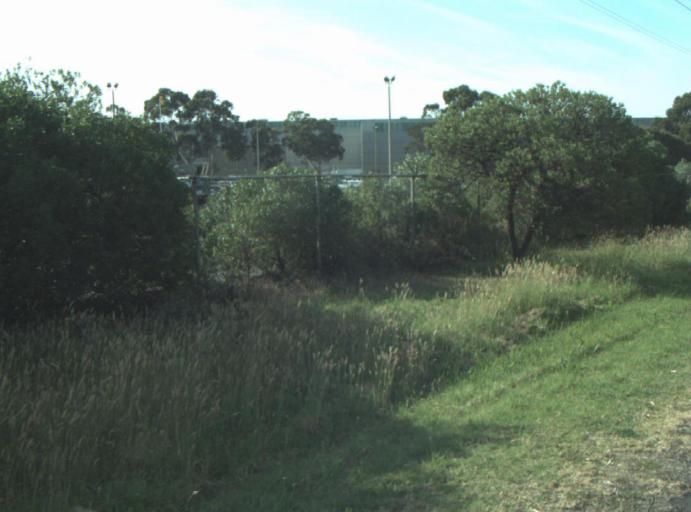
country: AU
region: Victoria
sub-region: Greater Geelong
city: East Geelong
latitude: -38.1361
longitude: 144.4204
